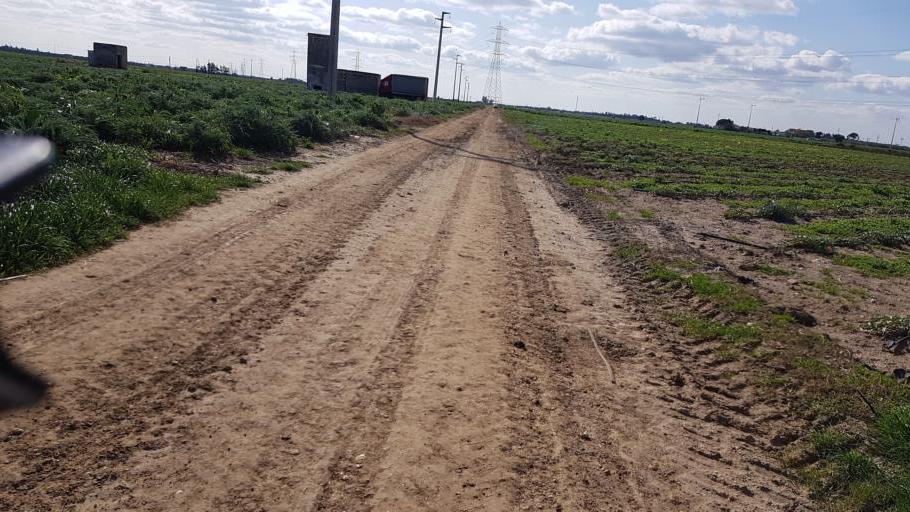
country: IT
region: Apulia
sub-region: Provincia di Brindisi
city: La Rosa
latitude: 40.5793
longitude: 17.9093
